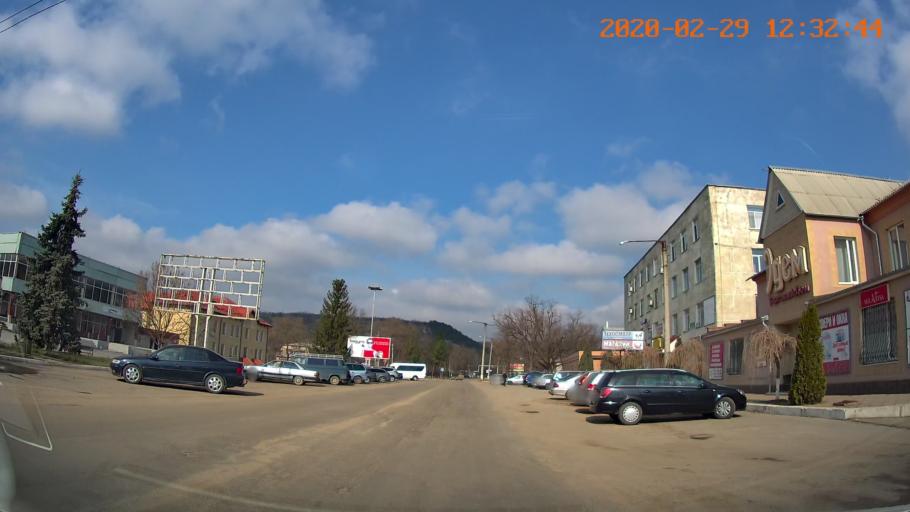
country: MD
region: Telenesti
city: Camenca
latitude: 48.0303
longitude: 28.7031
